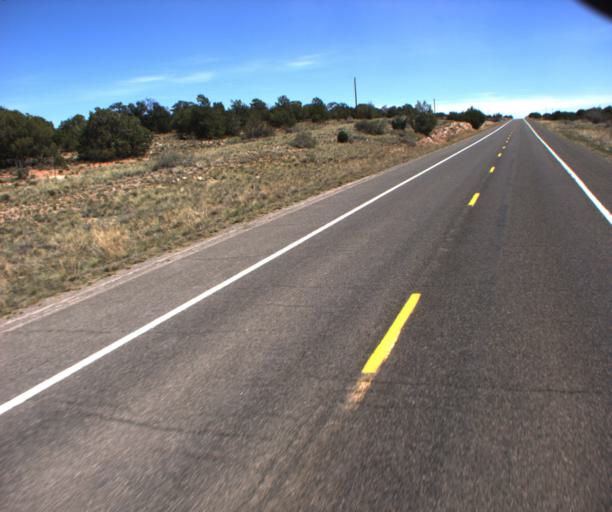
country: US
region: Arizona
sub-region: Mohave County
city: Peach Springs
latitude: 35.5496
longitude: -113.3033
